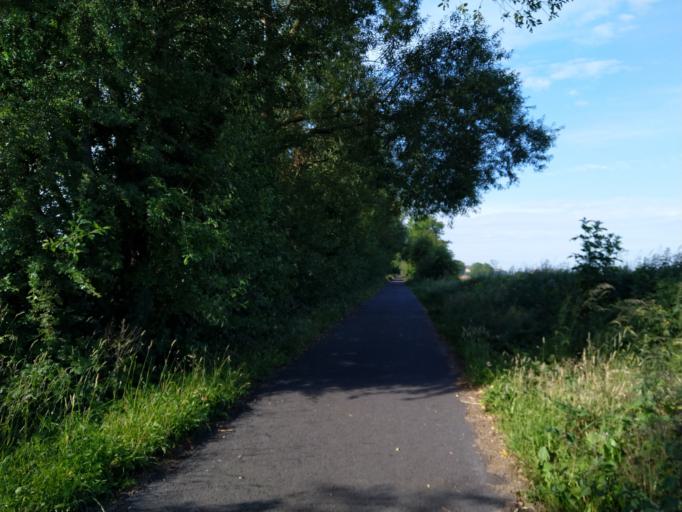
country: BE
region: Wallonia
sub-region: Province du Hainaut
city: Erquelinnes
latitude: 50.3556
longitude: 4.1088
